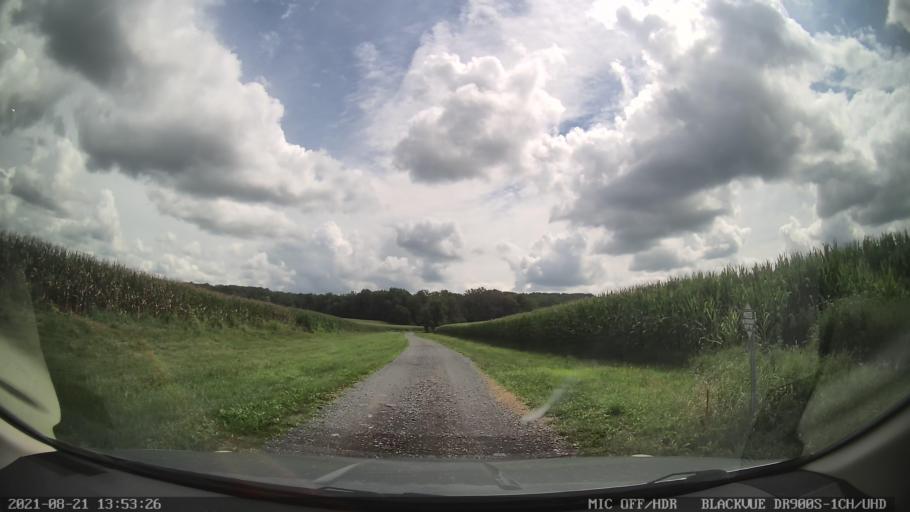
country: US
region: Pennsylvania
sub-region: Berks County
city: Fleetwood
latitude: 40.4695
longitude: -75.7799
